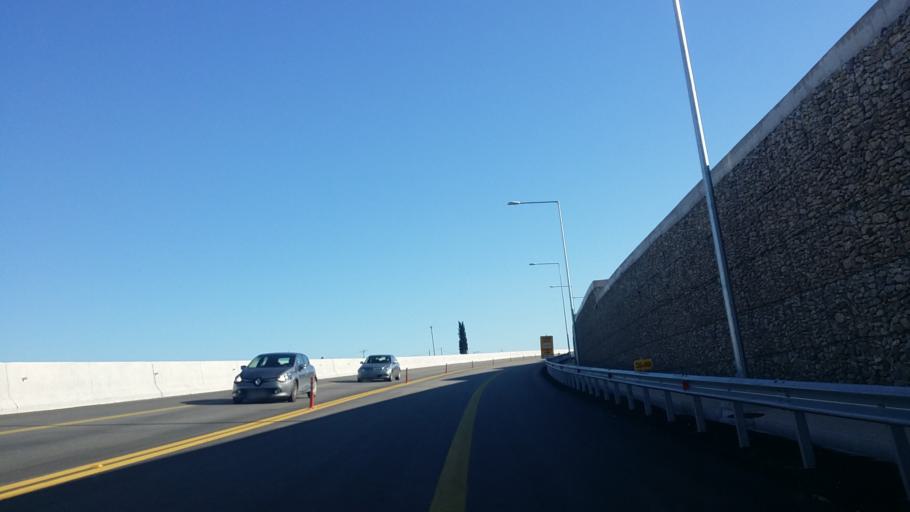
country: GR
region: West Greece
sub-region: Nomos Achaias
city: Ano Kastritsion
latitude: 38.3236
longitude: 21.8426
